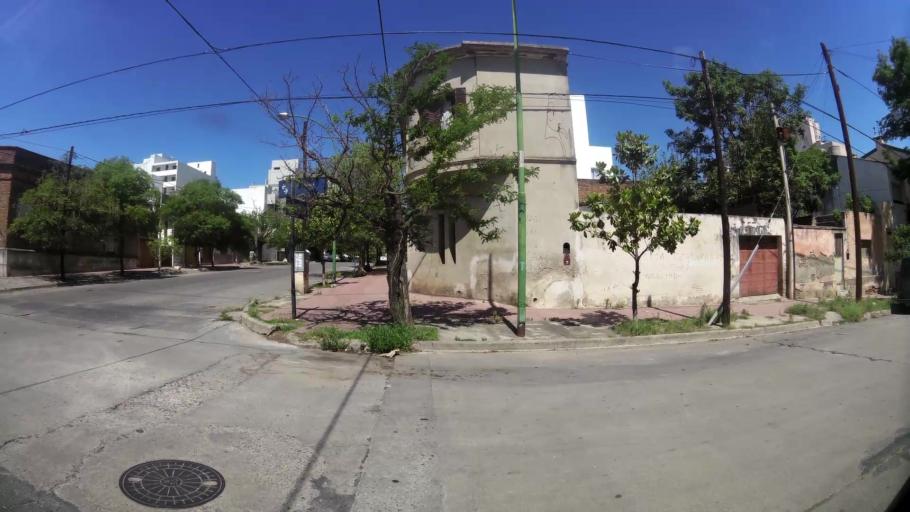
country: AR
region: Cordoba
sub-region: Departamento de Capital
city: Cordoba
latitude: -31.3976
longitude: -64.1924
